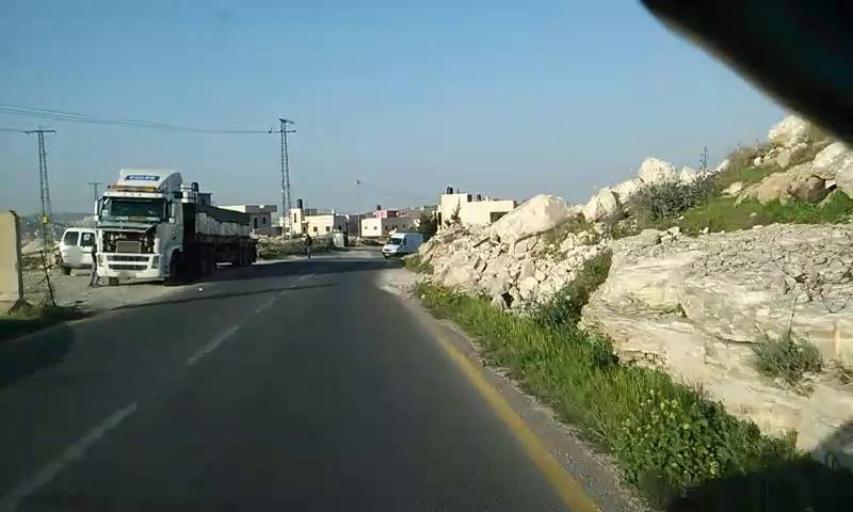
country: PS
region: West Bank
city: Jannatah
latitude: 31.6526
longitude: 35.2070
